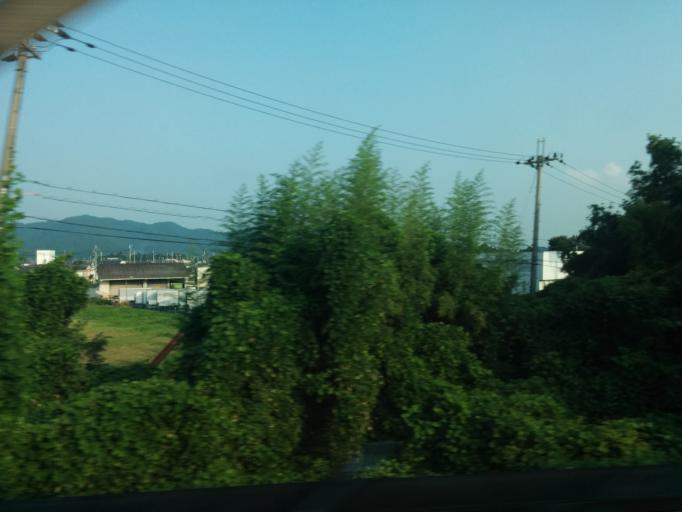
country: JP
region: Shiga Prefecture
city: Youkaichi
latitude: 35.1566
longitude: 136.1991
